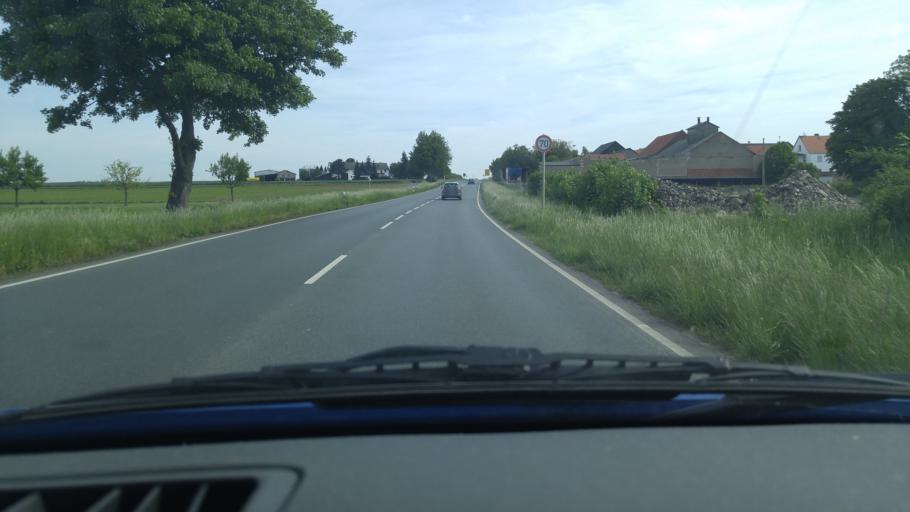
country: DE
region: Hesse
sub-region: Regierungsbezirk Darmstadt
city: Wolfersheim
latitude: 50.3813
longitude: 8.8057
